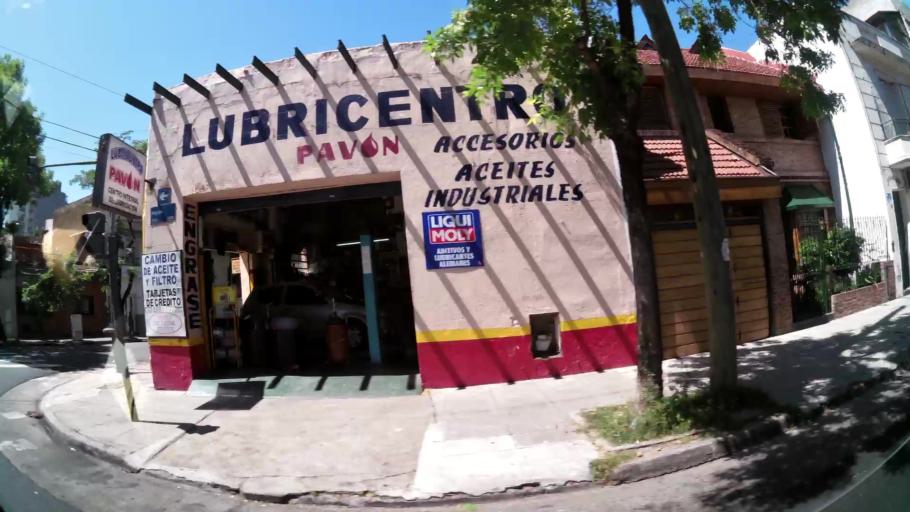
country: AR
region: Buenos Aires F.D.
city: Buenos Aires
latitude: -34.6293
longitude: -58.4120
